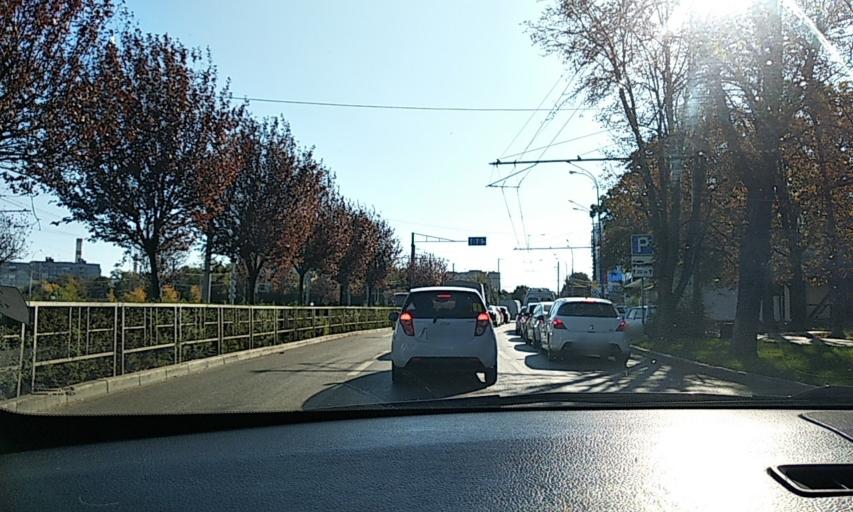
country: RU
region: Krasnodarskiy
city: Pashkovskiy
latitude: 45.0157
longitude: 39.0454
